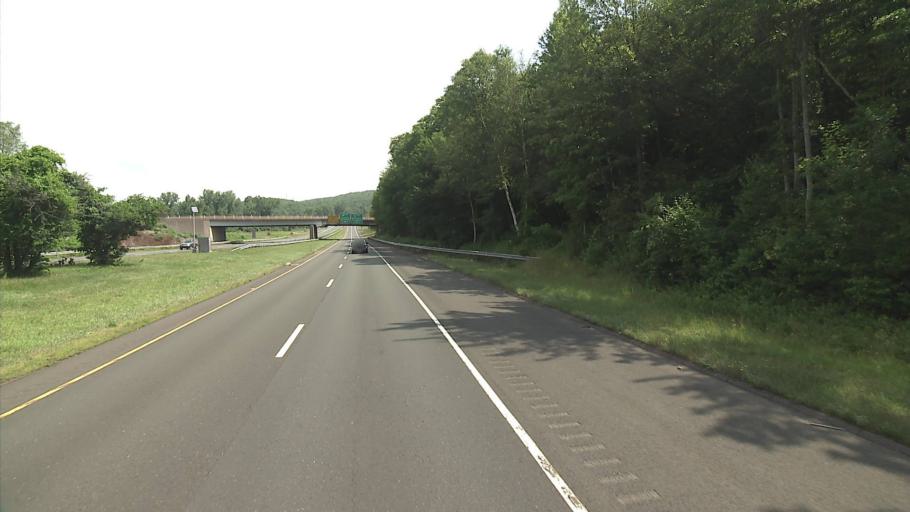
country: US
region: Connecticut
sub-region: Hartford County
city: Manchester
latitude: 41.7843
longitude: -72.4554
